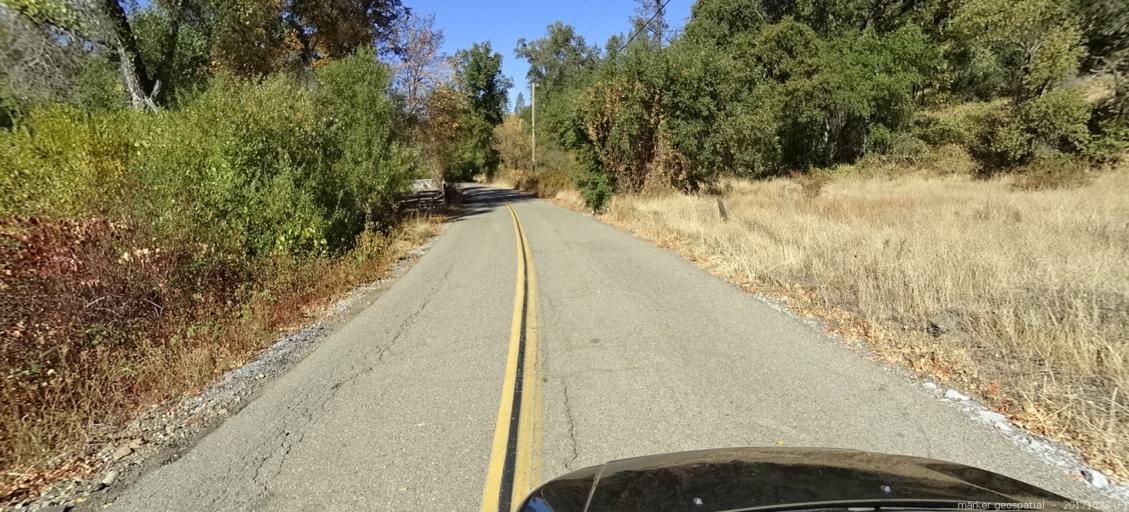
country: US
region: California
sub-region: Shasta County
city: Bella Vista
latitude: 40.7466
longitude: -122.0190
